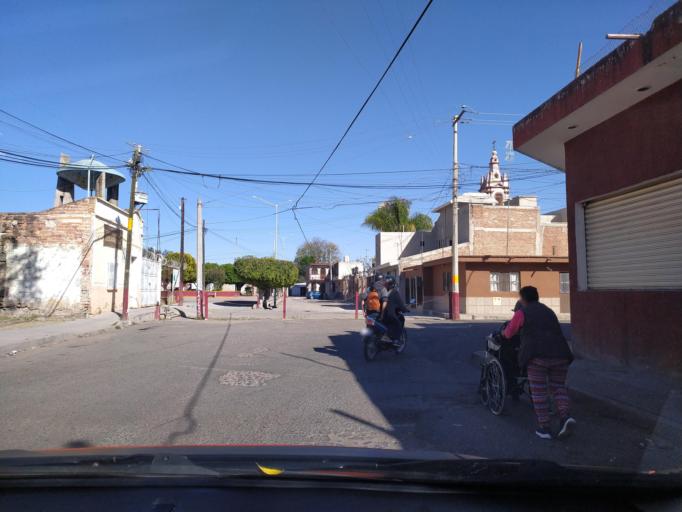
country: MX
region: Guanajuato
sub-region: San Francisco del Rincon
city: Fraccionamiento la Mezquitera
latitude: 21.0236
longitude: -101.8322
